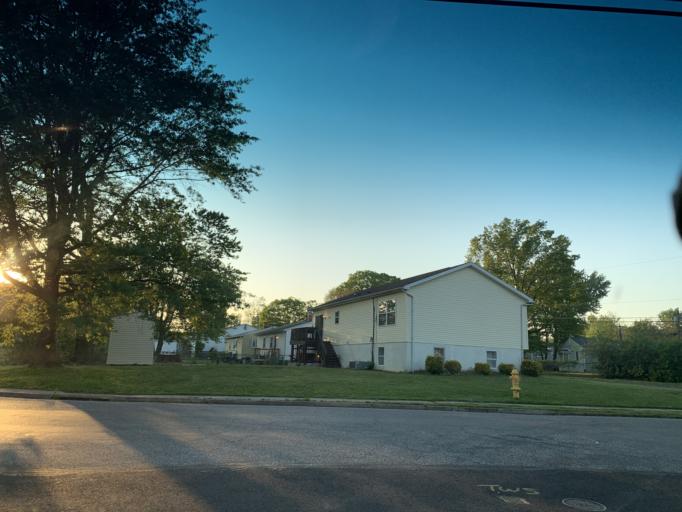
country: US
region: Maryland
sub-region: Harford County
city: Aberdeen
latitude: 39.5037
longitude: -76.1774
